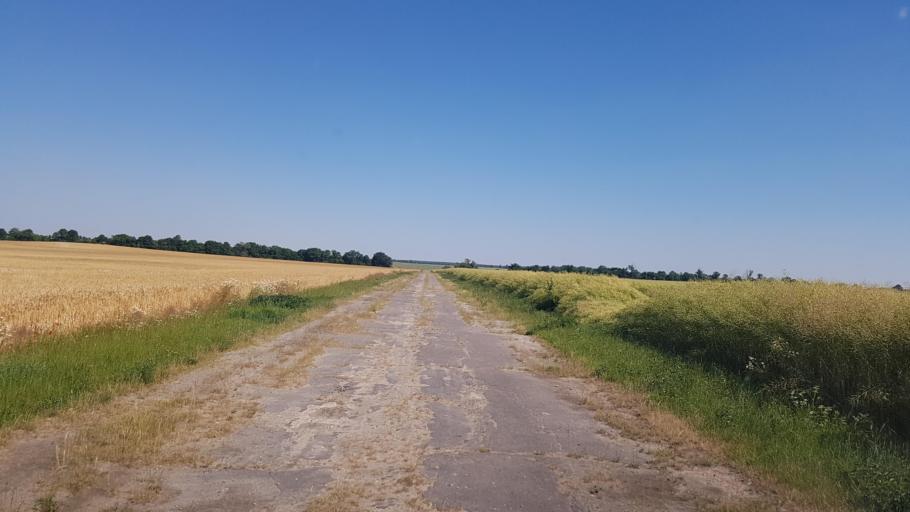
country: DE
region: Saxony-Anhalt
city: Seyda
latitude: 51.9653
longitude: 12.8920
